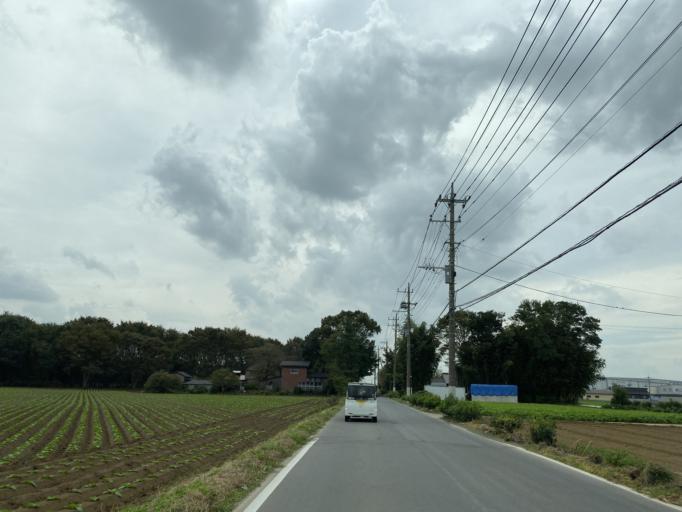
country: JP
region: Ibaraki
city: Mitsukaido
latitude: 36.0112
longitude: 140.0441
